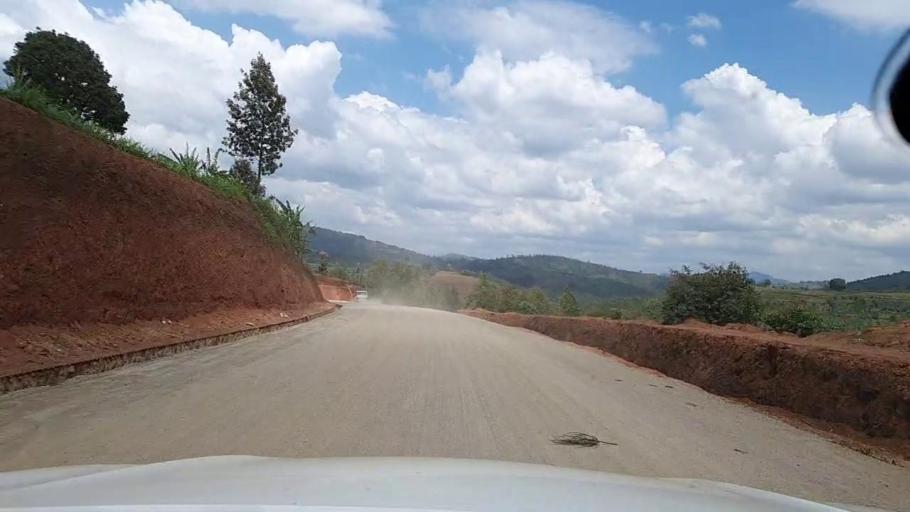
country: RW
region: Southern Province
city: Butare
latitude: -2.6965
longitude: 29.5609
